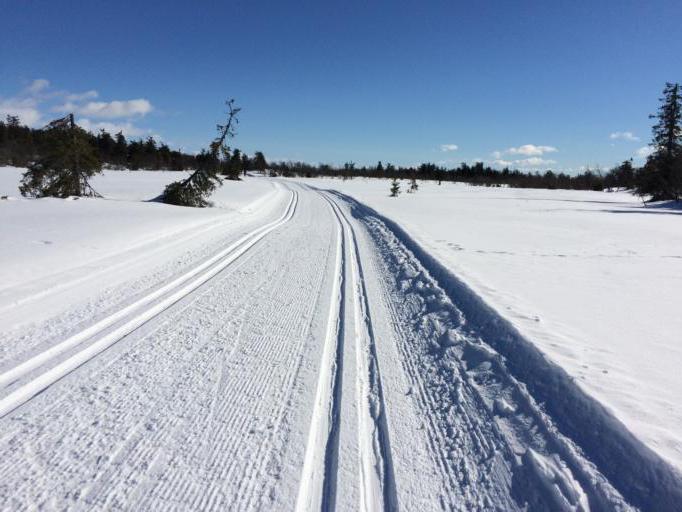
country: NO
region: Oppland
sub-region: Gausdal
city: Segalstad bru
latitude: 61.3086
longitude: 10.0988
